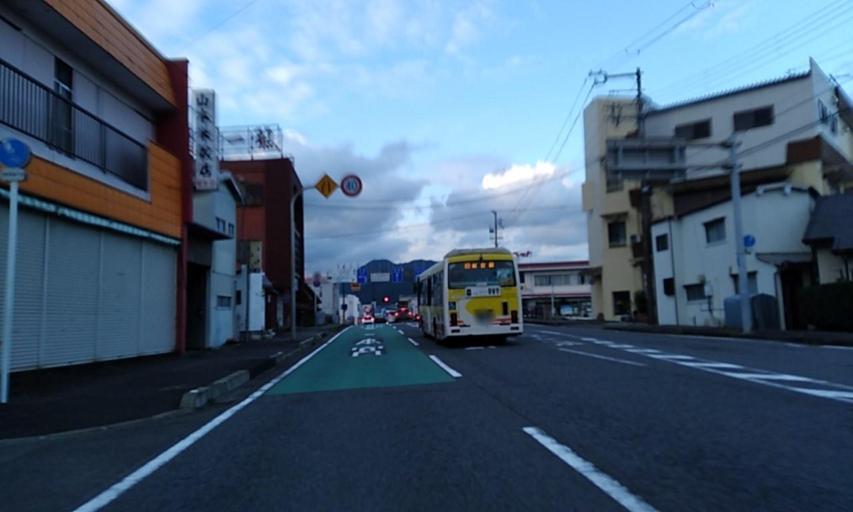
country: JP
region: Wakayama
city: Shingu
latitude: 33.7180
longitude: 135.9871
